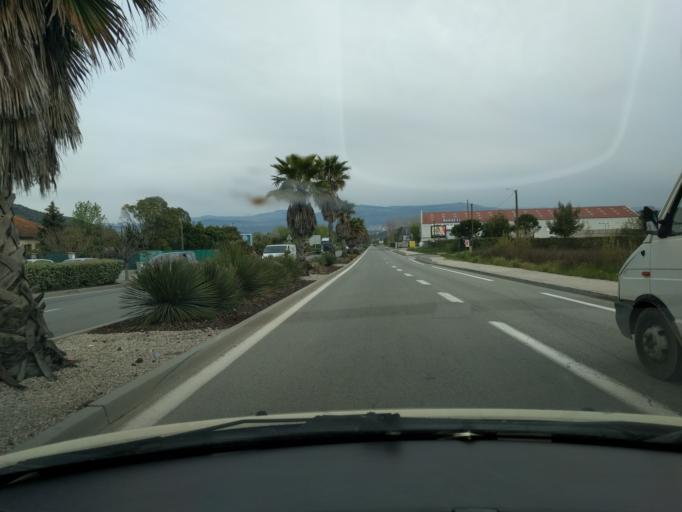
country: FR
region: Provence-Alpes-Cote d'Azur
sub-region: Departement des Alpes-Maritimes
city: Mandelieu-la-Napoule
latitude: 43.5615
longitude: 6.9507
